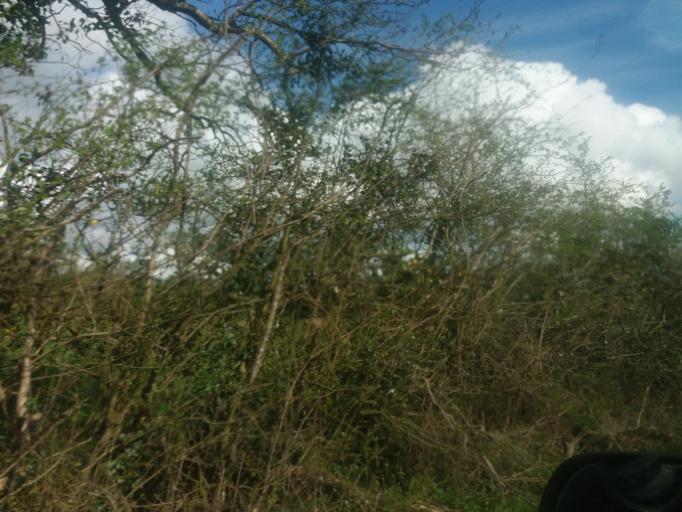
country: IE
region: Ulster
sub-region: An Cabhan
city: Ballyconnell
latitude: 54.1654
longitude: -7.5107
